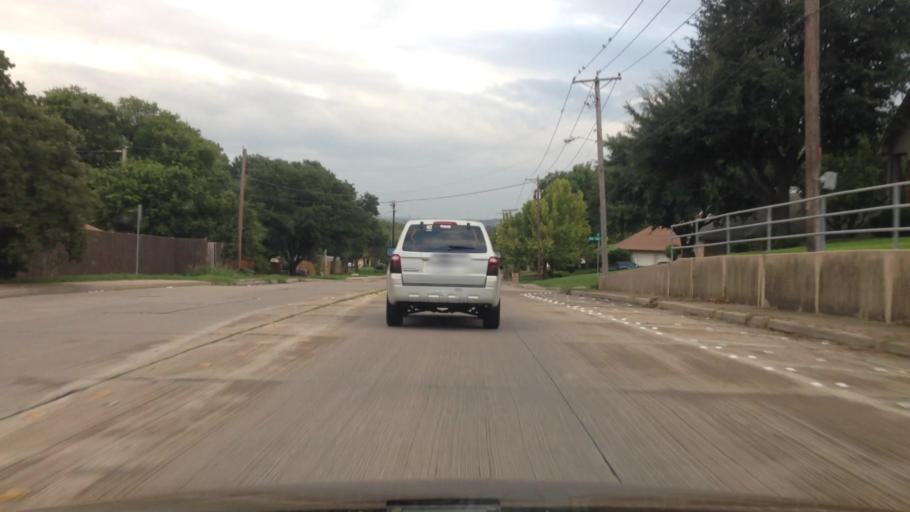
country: US
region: Texas
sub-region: Johnson County
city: Burleson
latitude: 32.5536
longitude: -97.3372
